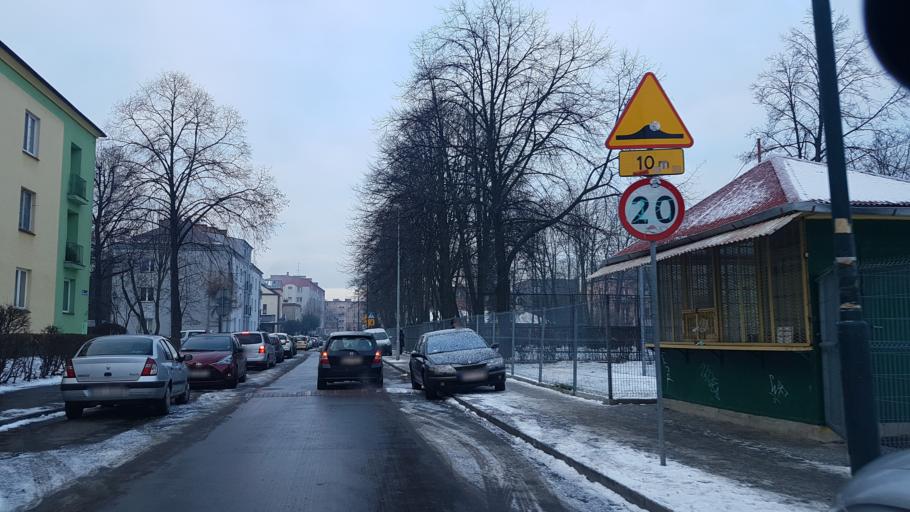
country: PL
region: Lesser Poland Voivodeship
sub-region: Powiat nowosadecki
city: Nowy Sacz
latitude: 49.6126
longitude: 20.7031
